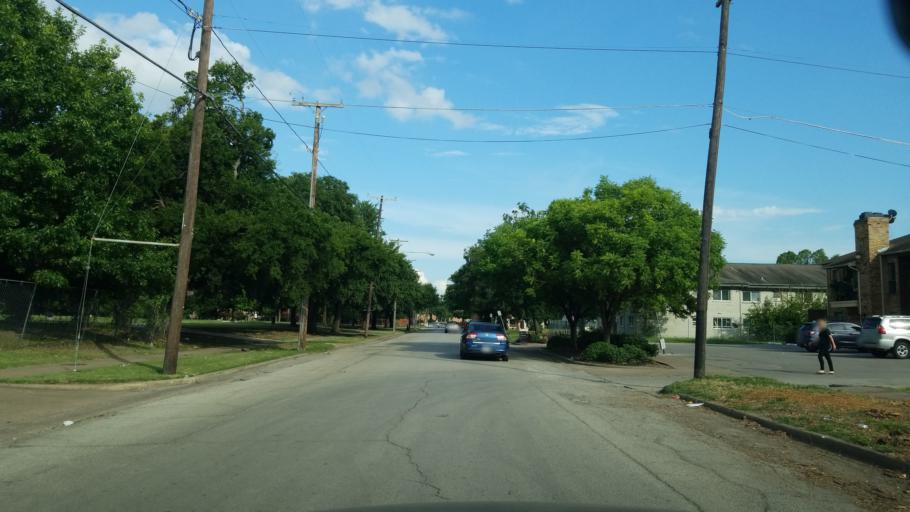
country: US
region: Texas
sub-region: Dallas County
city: Highland Park
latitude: 32.8068
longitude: -96.7725
